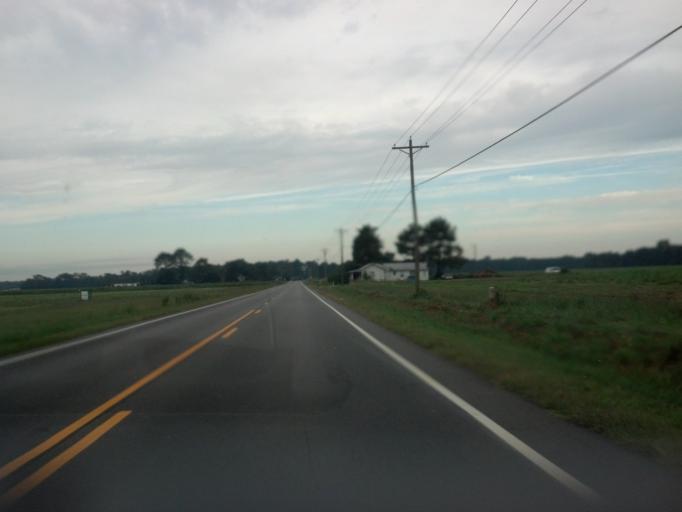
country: US
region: North Carolina
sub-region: Greene County
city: Maury
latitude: 35.4625
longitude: -77.5104
